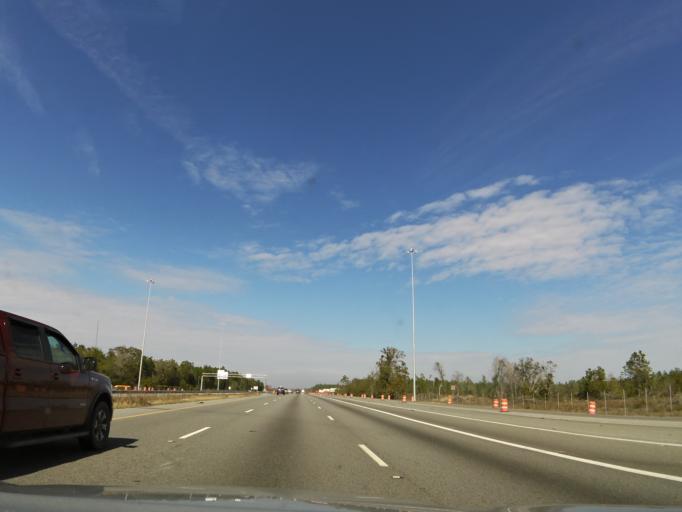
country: US
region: Georgia
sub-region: McIntosh County
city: Darien
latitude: 31.3990
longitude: -81.4478
